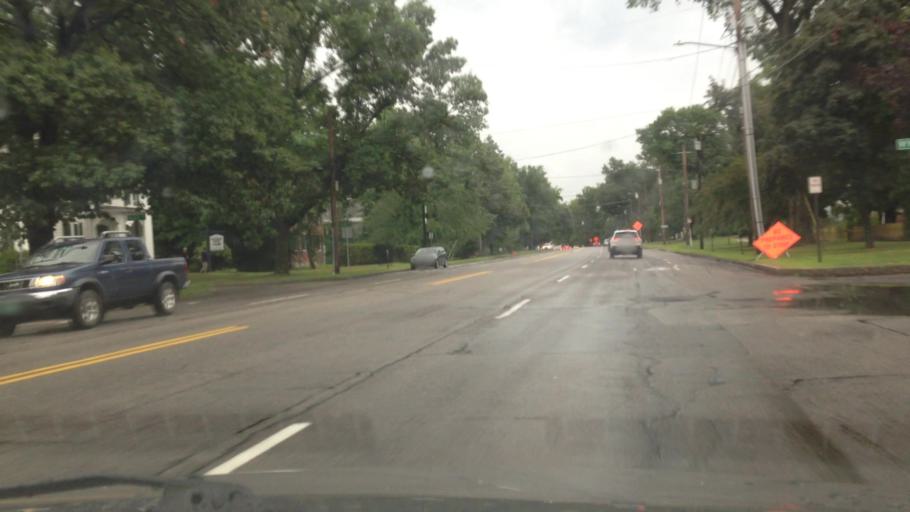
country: US
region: New Hampshire
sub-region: Cheshire County
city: Keene
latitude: 42.9256
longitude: -72.2772
